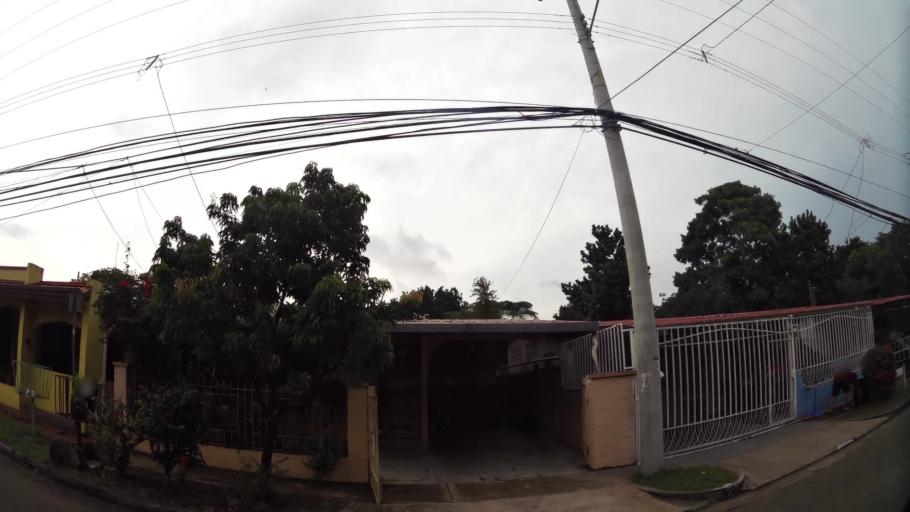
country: PA
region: Panama
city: Panama
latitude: 9.0147
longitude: -79.5381
